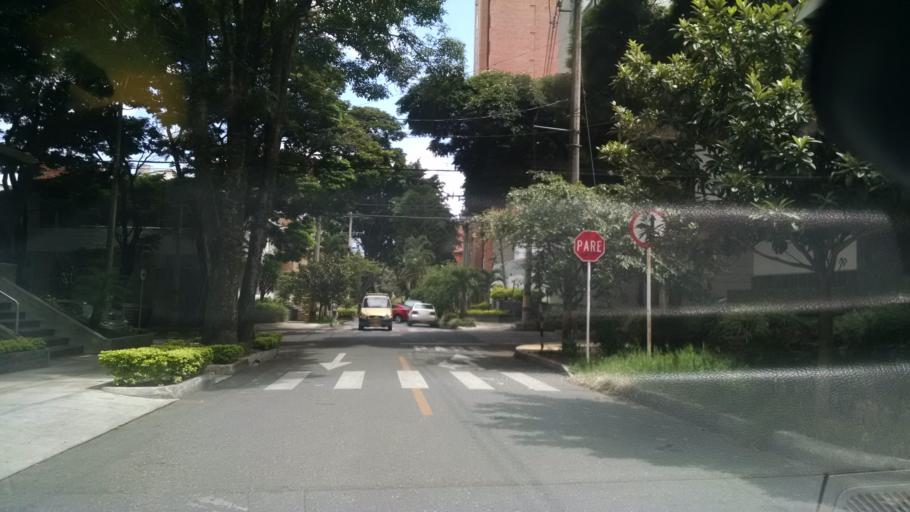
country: CO
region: Antioquia
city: Medellin
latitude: 6.2420
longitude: -75.5932
